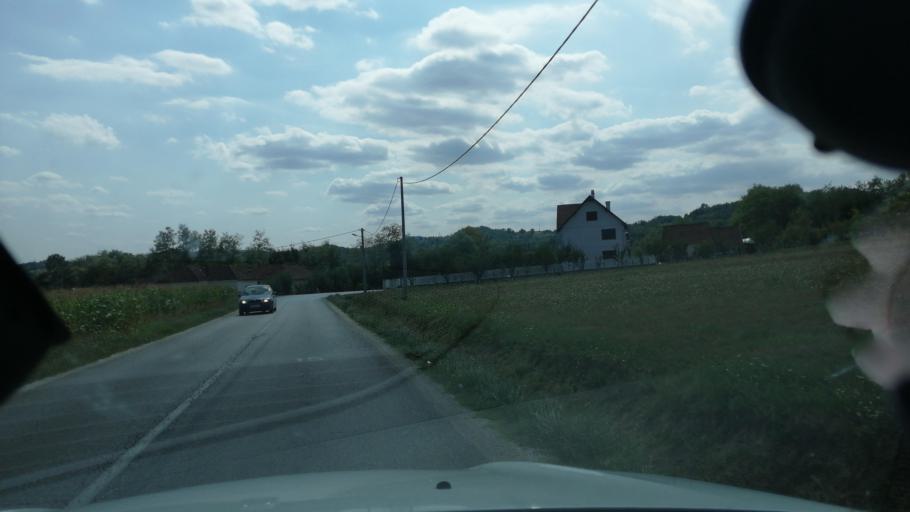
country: RS
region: Central Serbia
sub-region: Moravicki Okrug
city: Lucani
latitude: 43.7946
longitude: 20.2544
